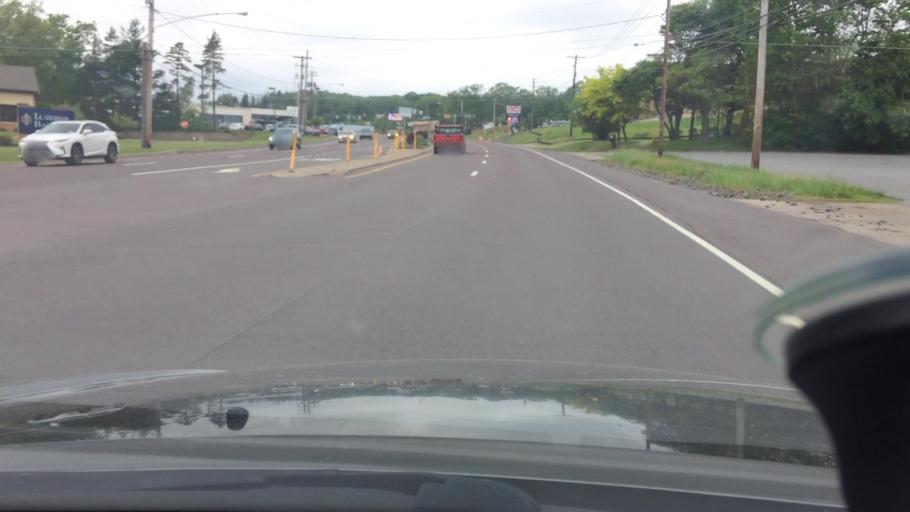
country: US
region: Pennsylvania
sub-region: Luzerne County
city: West Hazleton
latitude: 40.9761
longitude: -76.0111
